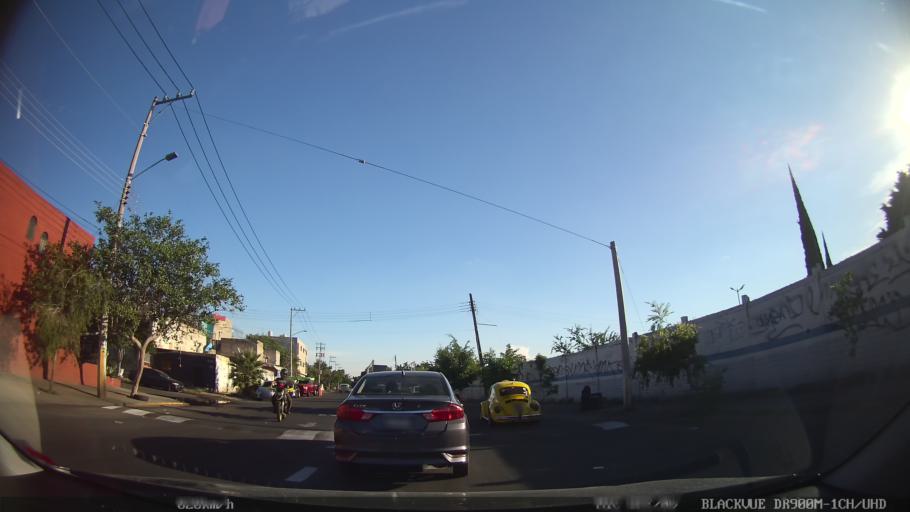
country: MX
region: Jalisco
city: Tlaquepaque
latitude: 20.7016
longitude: -103.3009
